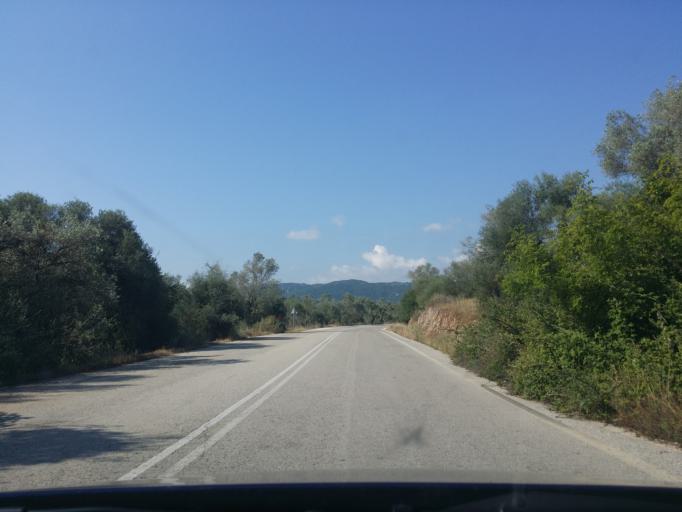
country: GR
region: West Greece
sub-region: Nomos Aitolias kai Akarnanias
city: Stanos
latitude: 38.7755
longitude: 21.1844
